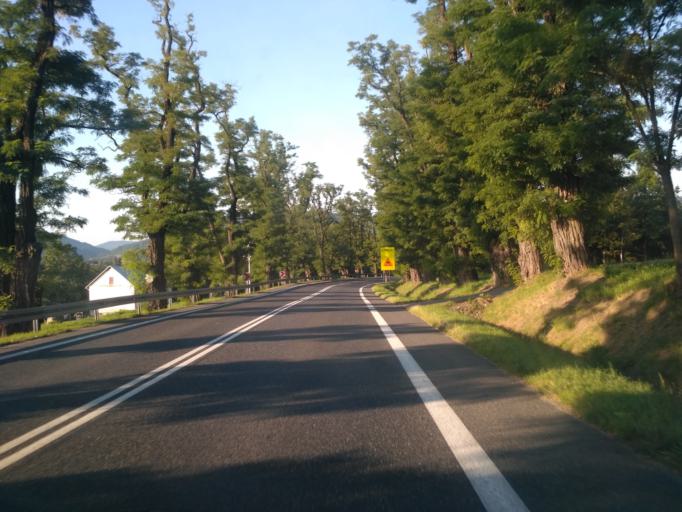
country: PL
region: Subcarpathian Voivodeship
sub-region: Powiat krosnienski
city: Dukla
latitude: 49.5634
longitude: 21.6908
